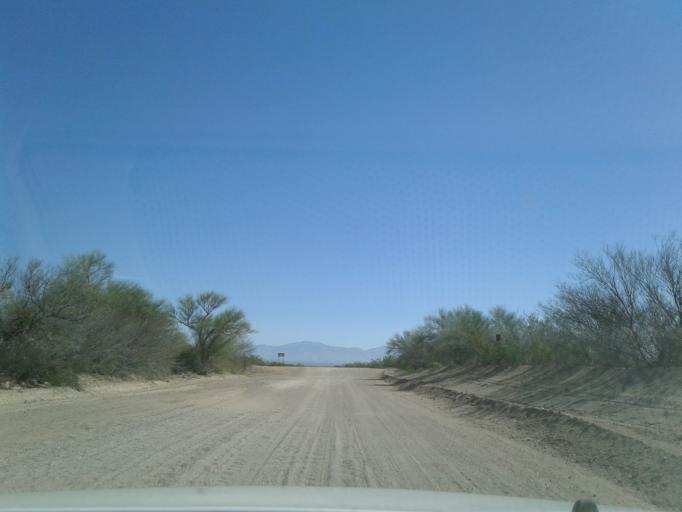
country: US
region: Arizona
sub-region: Pima County
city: Avra Valley
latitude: 32.4293
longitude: -111.3618
